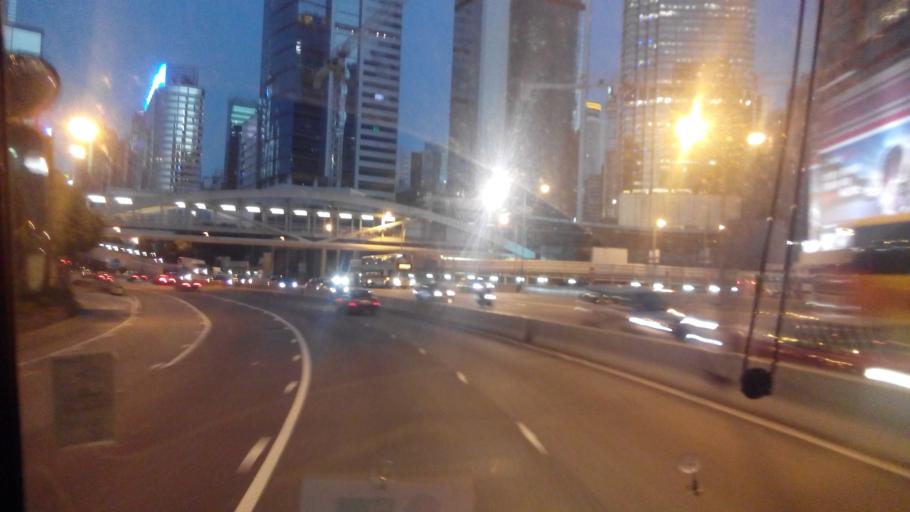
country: HK
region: Central and Western
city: Central
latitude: 22.2796
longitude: 114.1652
